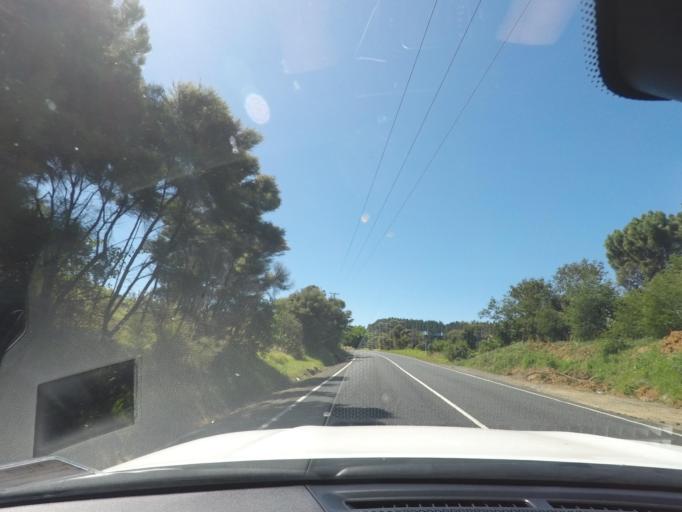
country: NZ
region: Auckland
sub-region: Auckland
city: Parakai
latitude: -36.5827
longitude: 174.3301
